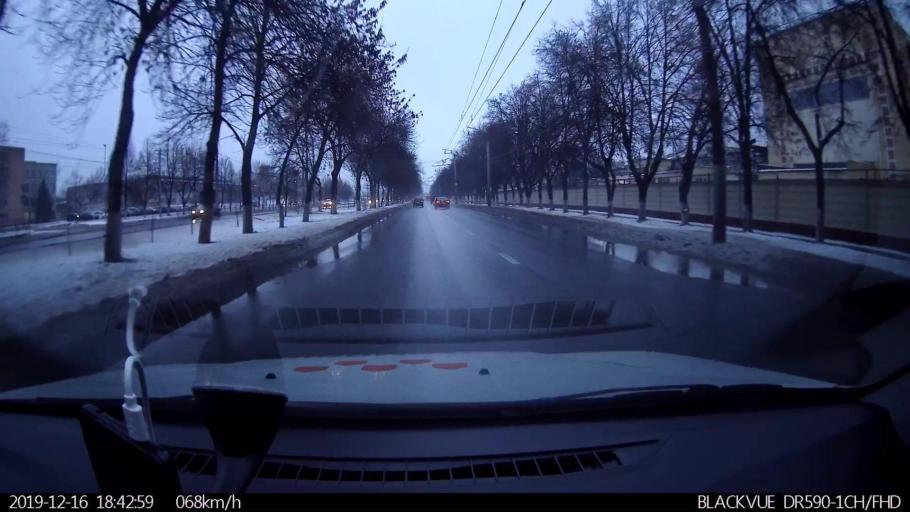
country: RU
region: Nizjnij Novgorod
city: Nizhniy Novgorod
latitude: 56.2540
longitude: 43.8966
